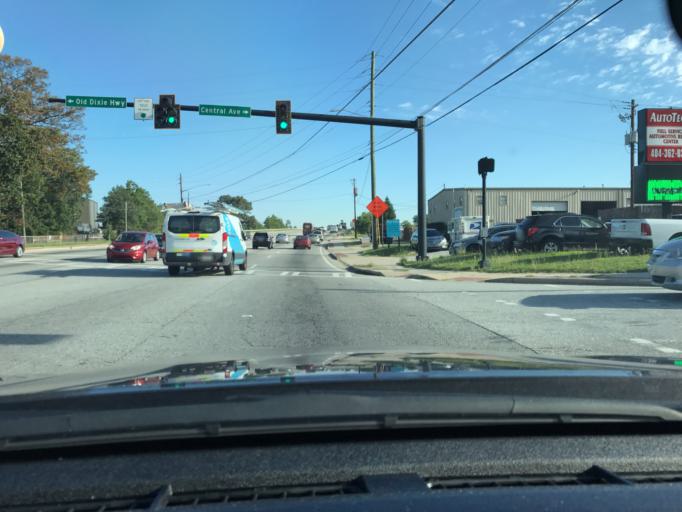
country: US
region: Georgia
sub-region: Clayton County
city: Forest Park
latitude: 33.6236
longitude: -84.3841
